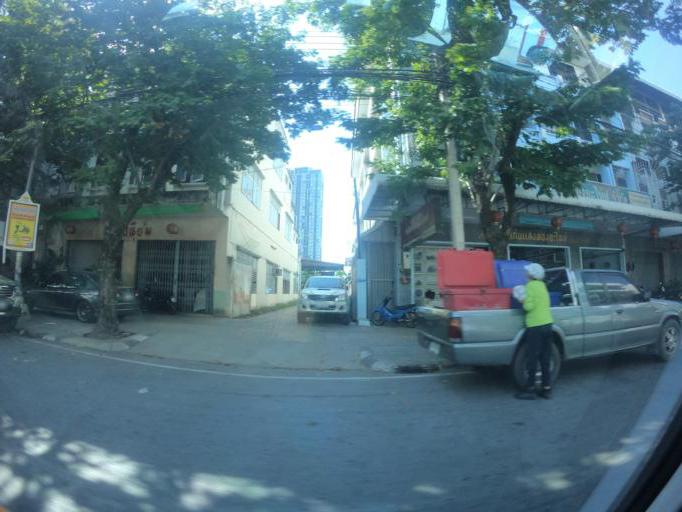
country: TH
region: Khon Kaen
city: Sam Sung
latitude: 16.4829
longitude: 102.9627
